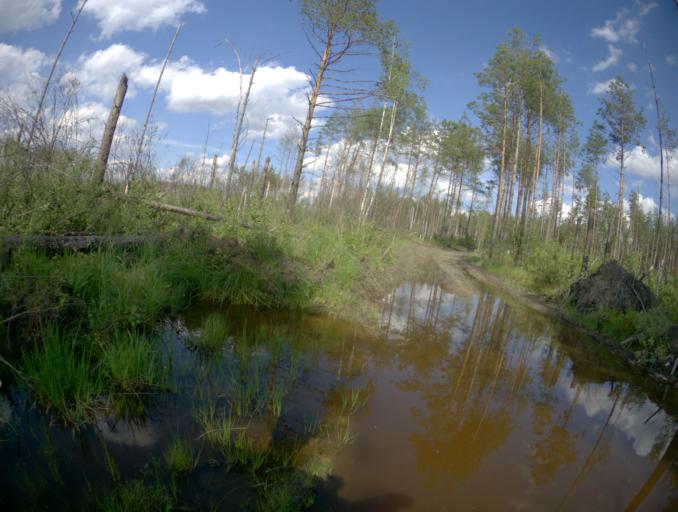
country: RU
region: Vladimir
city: Velikodvorskiy
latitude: 55.3170
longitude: 40.9210
